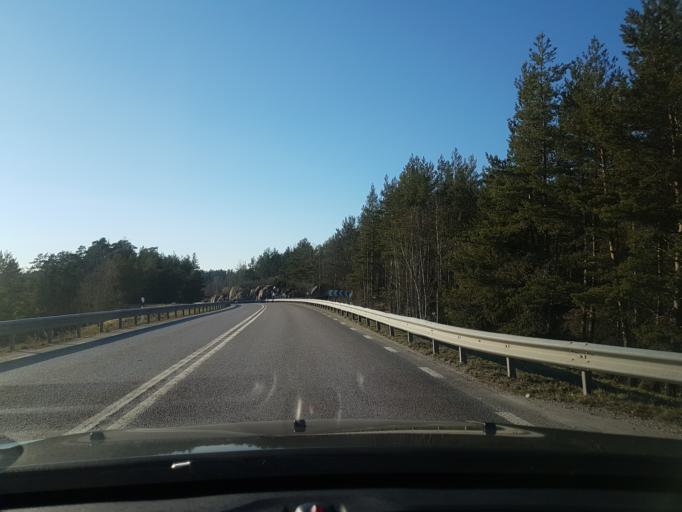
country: SE
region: Uppsala
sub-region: Enkopings Kommun
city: Orsundsbro
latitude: 59.8609
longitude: 17.3698
